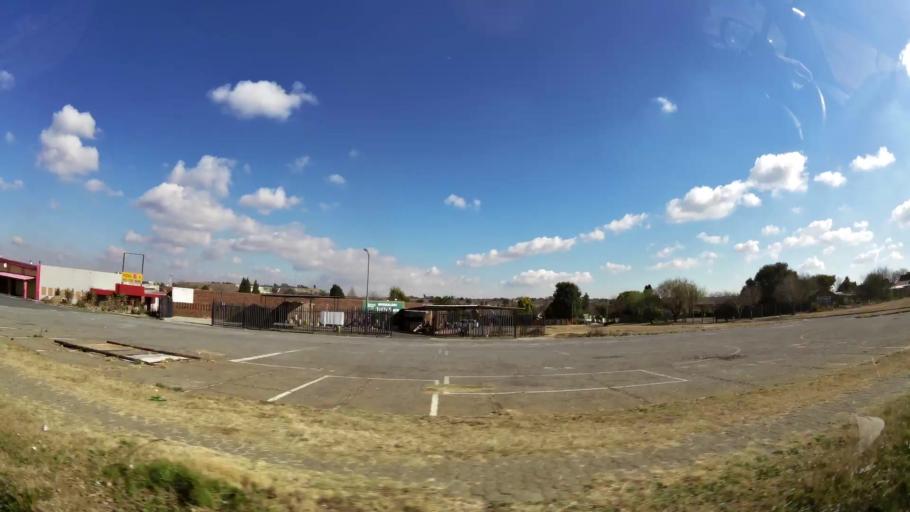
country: ZA
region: Gauteng
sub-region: City of Johannesburg Metropolitan Municipality
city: Roodepoort
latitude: -26.1417
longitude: 27.8268
